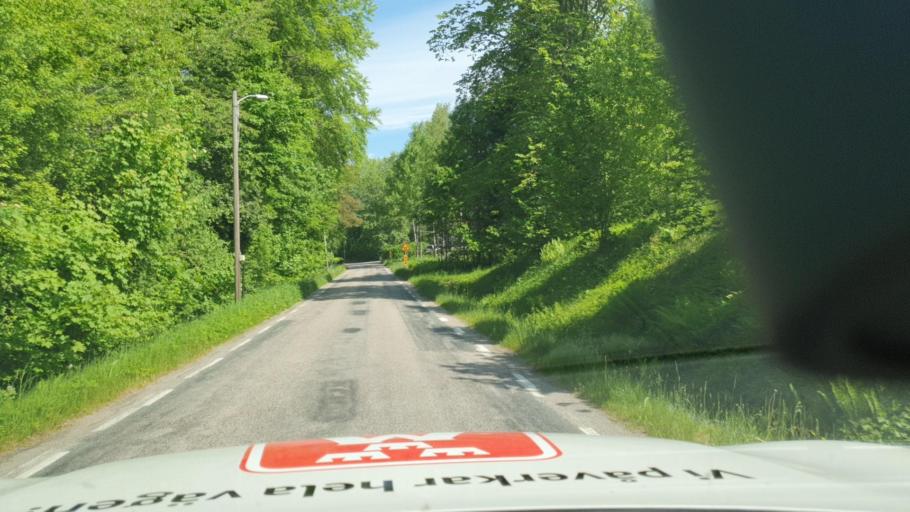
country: SE
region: Vaestra Goetaland
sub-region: Herrljunga Kommun
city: Herrljunga
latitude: 58.1060
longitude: 13.1091
